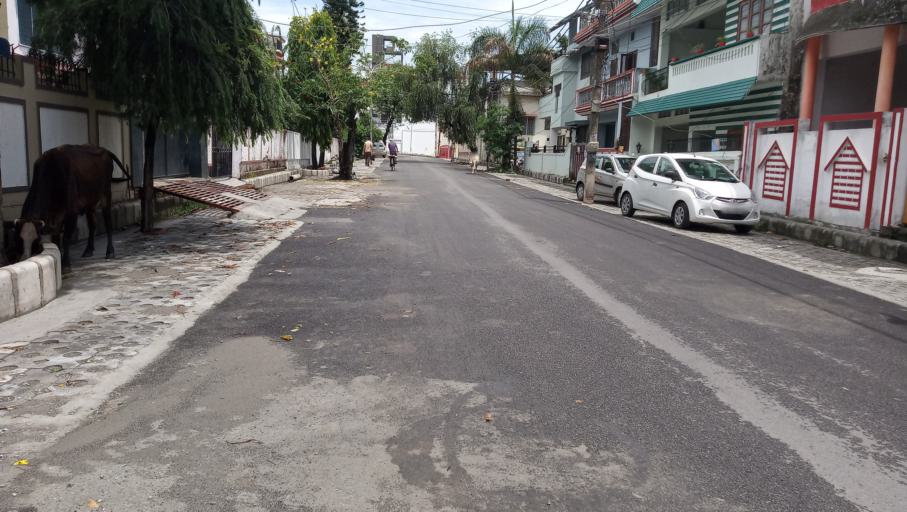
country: IN
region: Uttarakhand
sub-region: Dehradun
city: Dehradun
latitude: 30.3650
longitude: 78.0662
